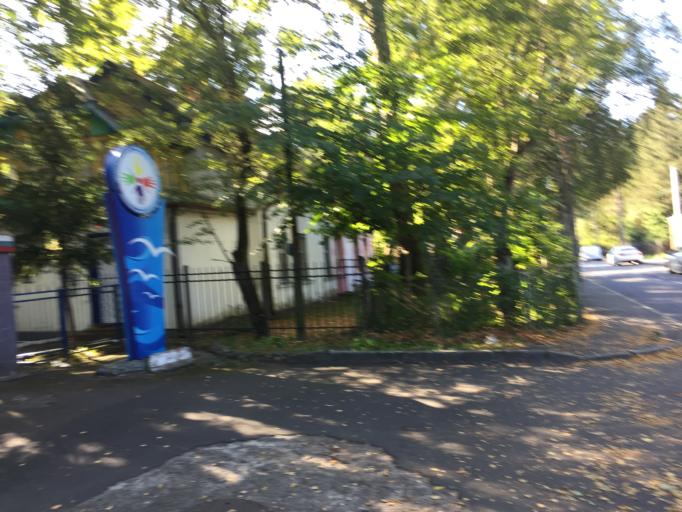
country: RU
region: Kaliningrad
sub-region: Gorod Svetlogorsk
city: Svetlogorsk
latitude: 54.9433
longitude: 20.1428
